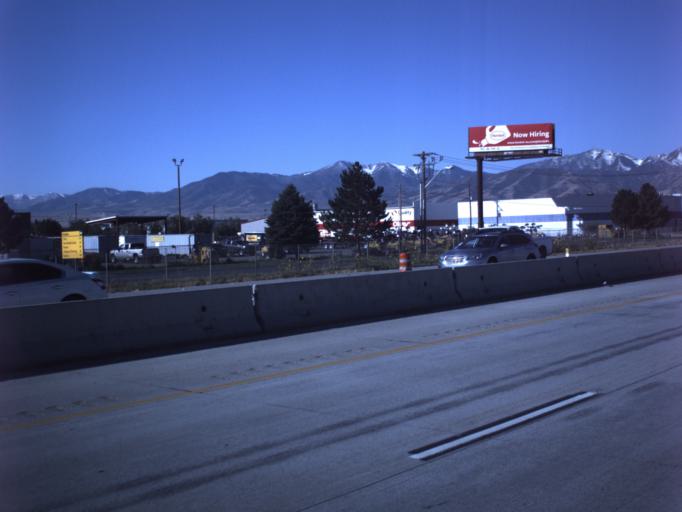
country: US
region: Utah
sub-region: Salt Lake County
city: West Valley City
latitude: 40.7259
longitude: -112.0104
